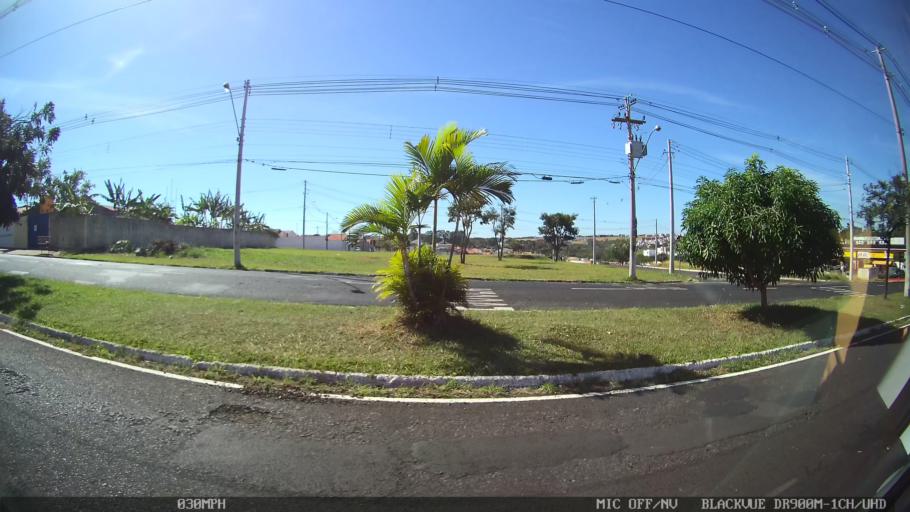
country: BR
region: Sao Paulo
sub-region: Franca
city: Franca
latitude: -20.5480
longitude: -47.3734
